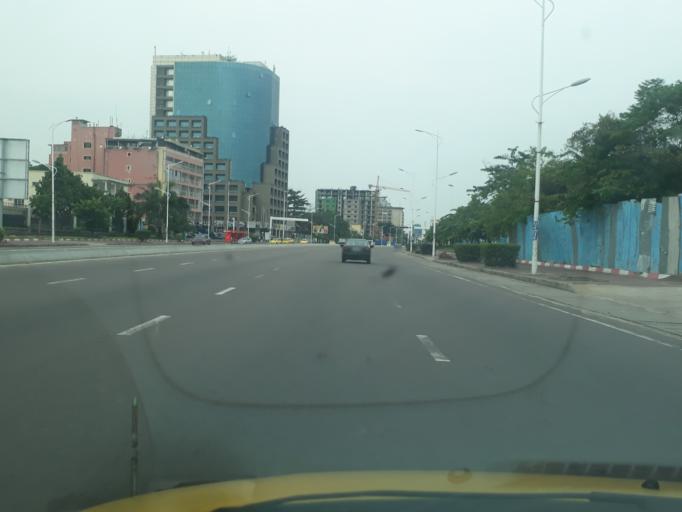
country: CD
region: Kinshasa
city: Kinshasa
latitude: -4.3182
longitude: 15.2777
